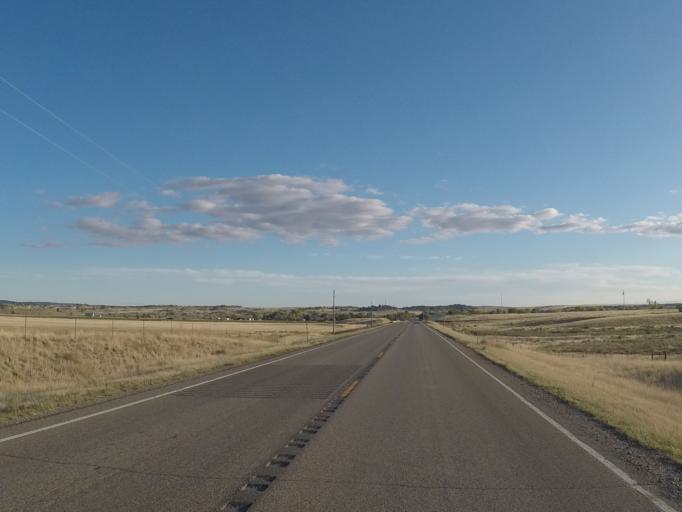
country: US
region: Montana
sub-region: Golden Valley County
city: Ryegate
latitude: 46.3035
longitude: -108.9380
